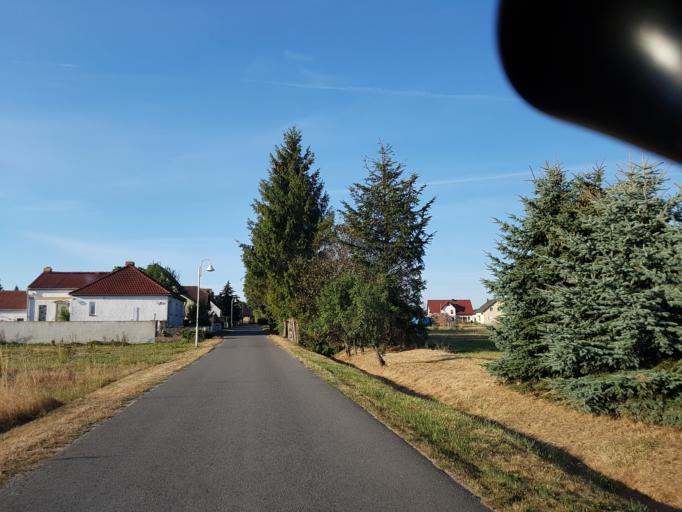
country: DE
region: Brandenburg
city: Plessa
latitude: 51.5322
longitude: 13.6349
